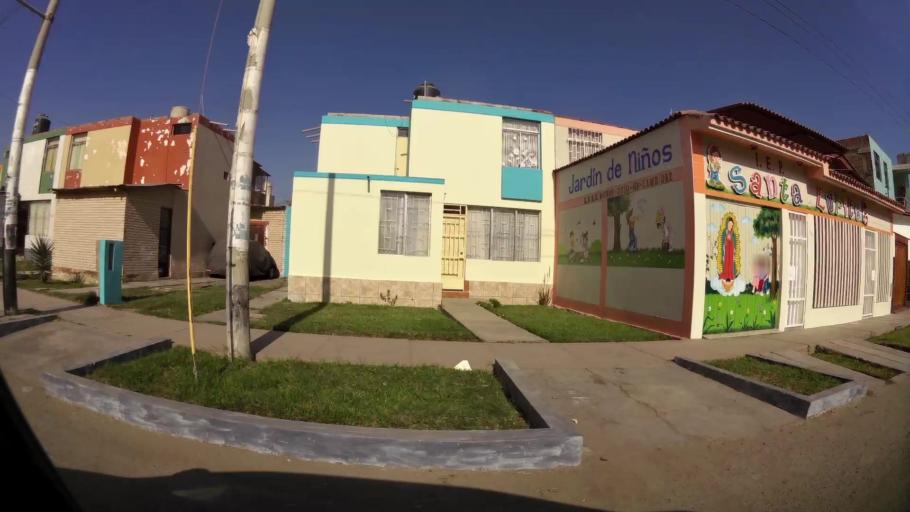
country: PE
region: Lambayeque
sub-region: Provincia de Chiclayo
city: Chiclayo
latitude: -6.7651
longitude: -79.8517
